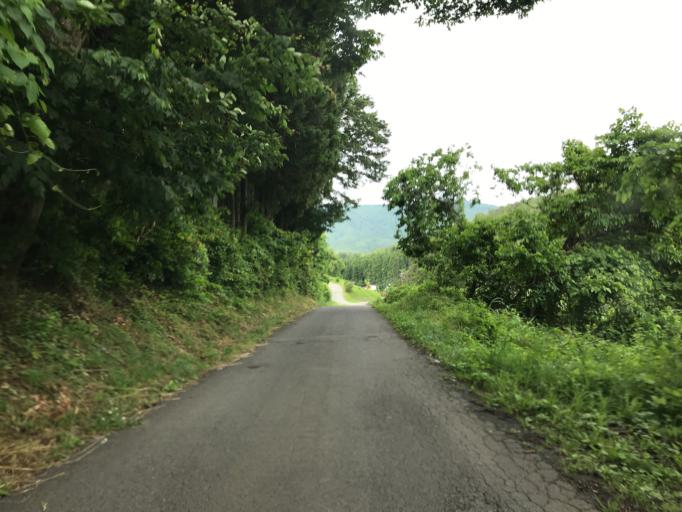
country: JP
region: Fukushima
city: Funehikimachi-funehiki
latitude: 37.5054
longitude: 140.6483
